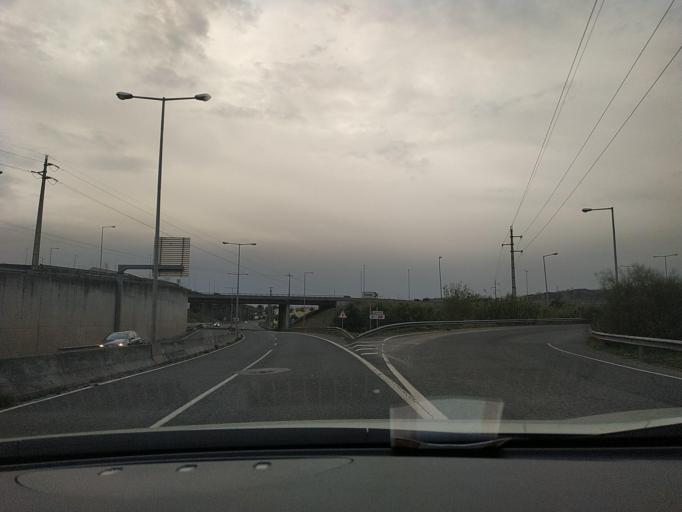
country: PT
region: Lisbon
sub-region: Loures
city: Santa Iria da Azoia
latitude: 38.8620
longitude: -9.1114
